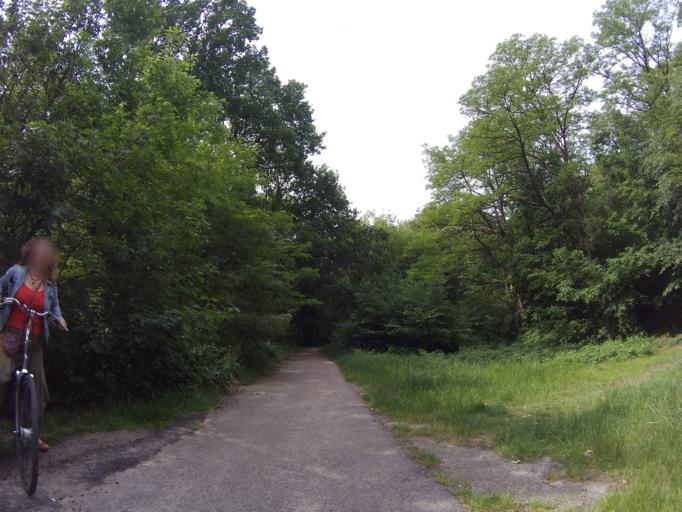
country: NL
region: Utrecht
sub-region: Gemeente Amersfoort
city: Amersfoort
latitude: 52.1414
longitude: 5.3694
